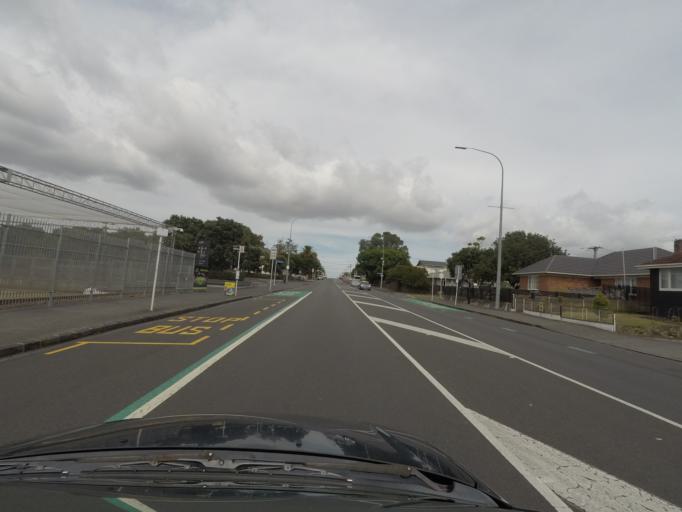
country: NZ
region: Auckland
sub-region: Auckland
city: Auckland
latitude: -36.8749
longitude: 174.7418
